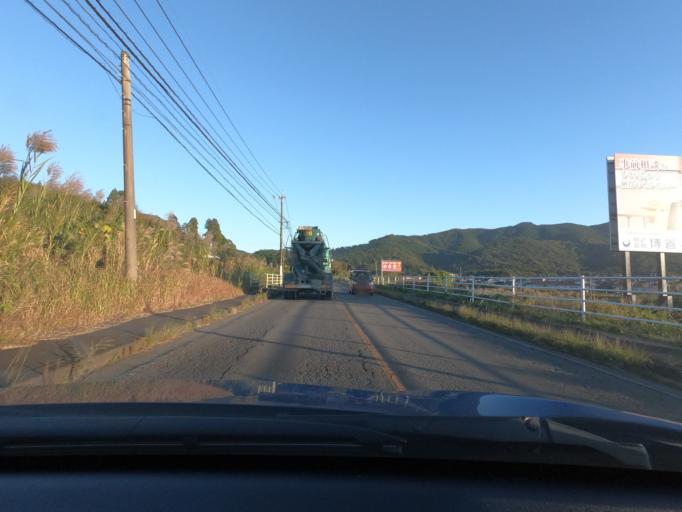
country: JP
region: Kagoshima
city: Satsumasendai
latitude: 31.8057
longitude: 130.3479
